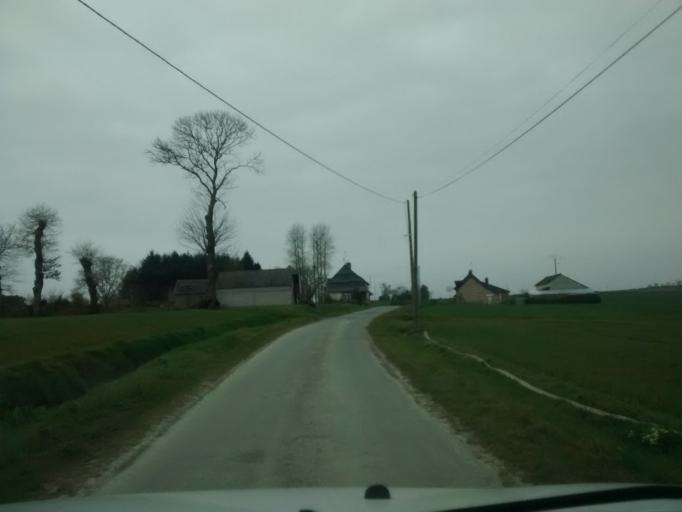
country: FR
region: Brittany
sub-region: Departement d'Ille-et-Vilaine
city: Bazouges-la-Perouse
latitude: 48.3879
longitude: -1.5824
